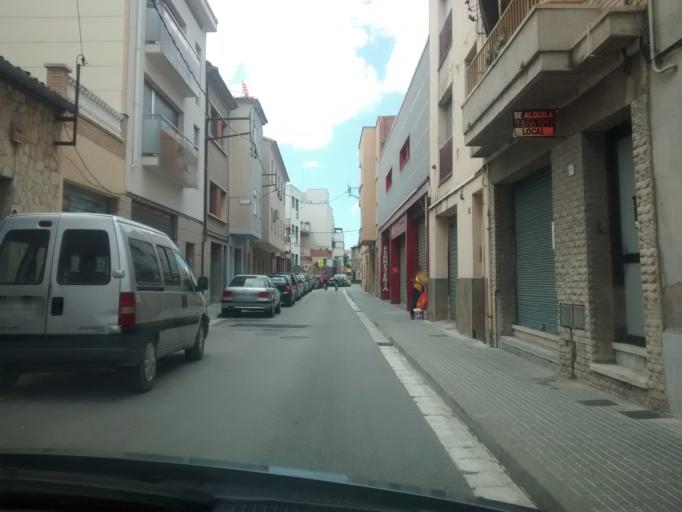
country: ES
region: Catalonia
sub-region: Provincia de Barcelona
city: Sant Vicenc dels Horts
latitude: 41.3921
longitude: 2.0123
